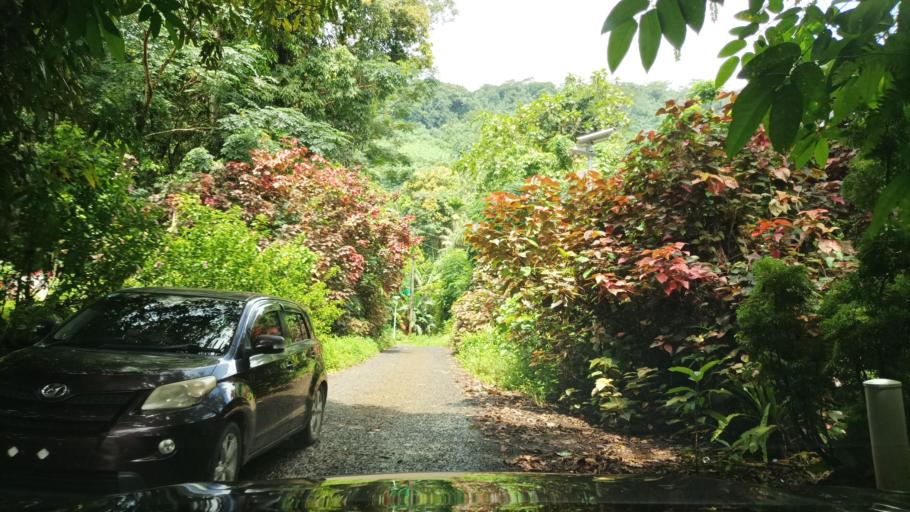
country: FM
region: Pohnpei
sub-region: Kolonia Municipality
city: Kolonia
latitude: 6.9612
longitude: 158.2243
